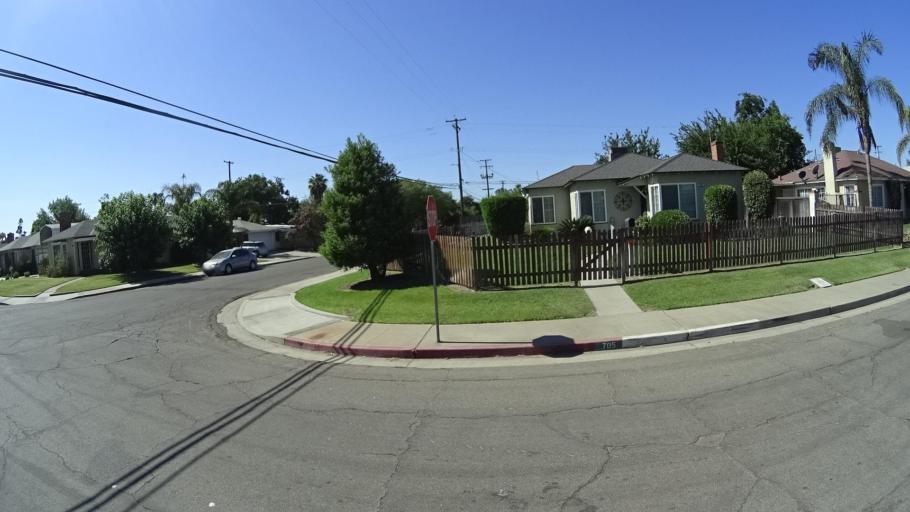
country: US
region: California
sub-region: Fresno County
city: Fresno
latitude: 36.7612
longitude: -119.8201
